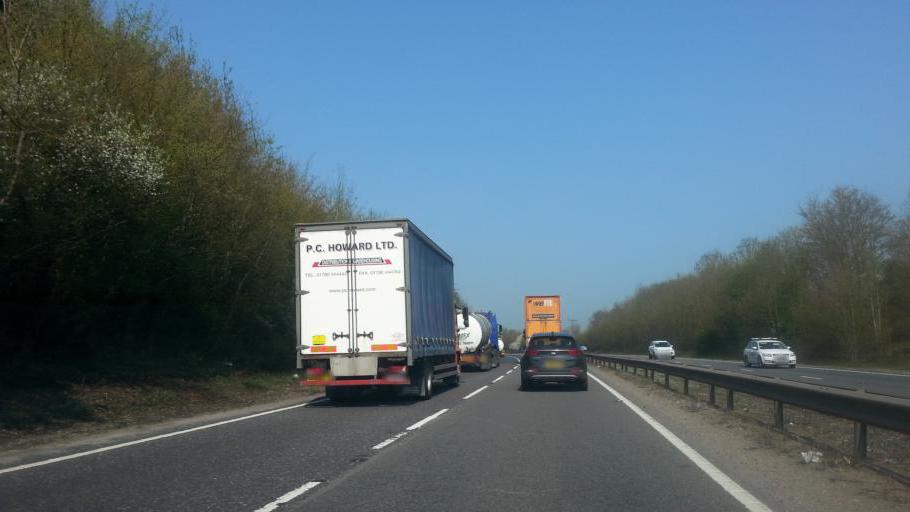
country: GB
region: England
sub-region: Suffolk
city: Stowmarket
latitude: 52.1918
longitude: 1.0157
